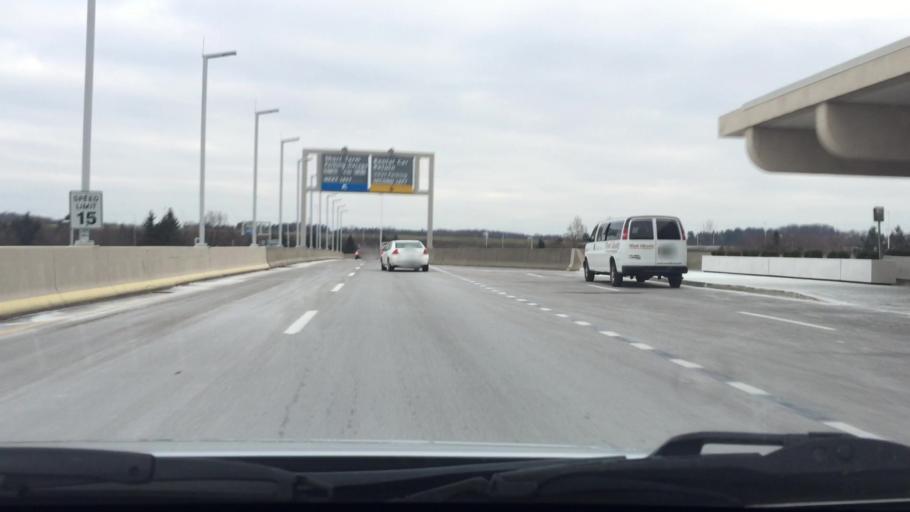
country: US
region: Pennsylvania
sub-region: Allegheny County
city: Carnot-Moon
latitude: 40.4966
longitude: -80.2566
